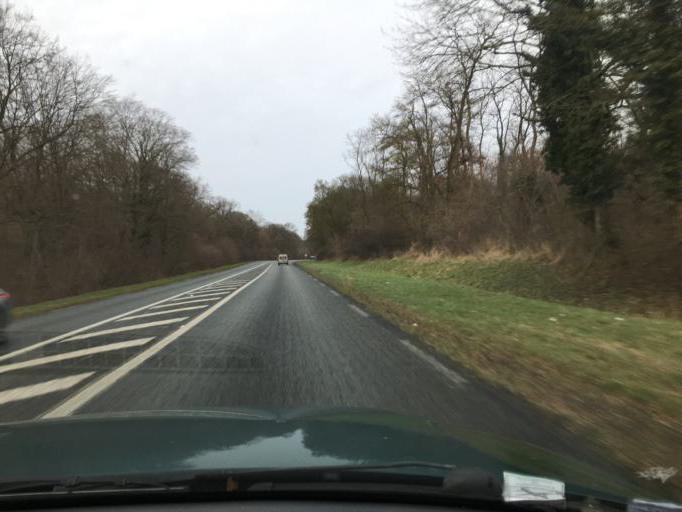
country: FR
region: Picardie
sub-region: Departement de l'Oise
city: Thiers-sur-Theve
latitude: 49.1586
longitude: 2.5520
